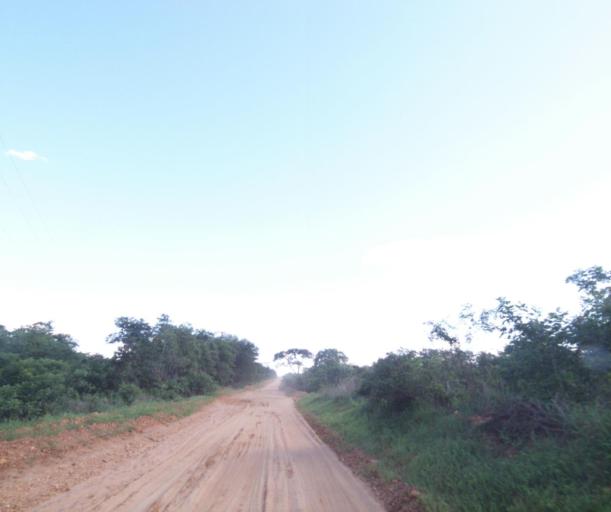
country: BR
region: Bahia
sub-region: Carinhanha
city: Carinhanha
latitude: -14.2231
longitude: -44.5341
